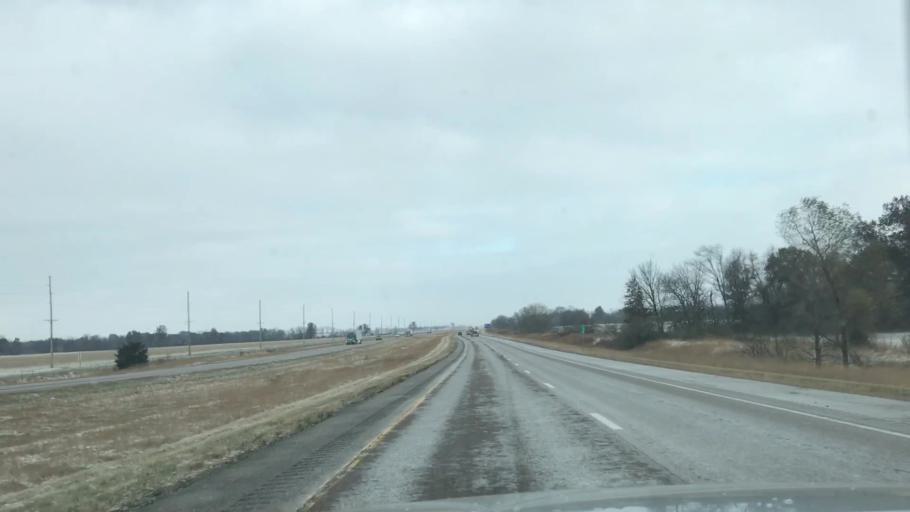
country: US
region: Illinois
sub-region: Macoupin County
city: Staunton
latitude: 38.9819
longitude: -89.7493
